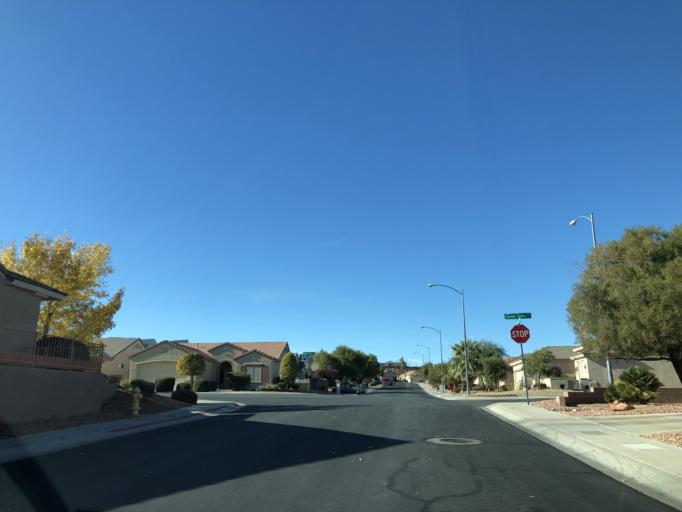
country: US
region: Nevada
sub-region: Clark County
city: Whitney
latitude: 36.0037
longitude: -115.0769
